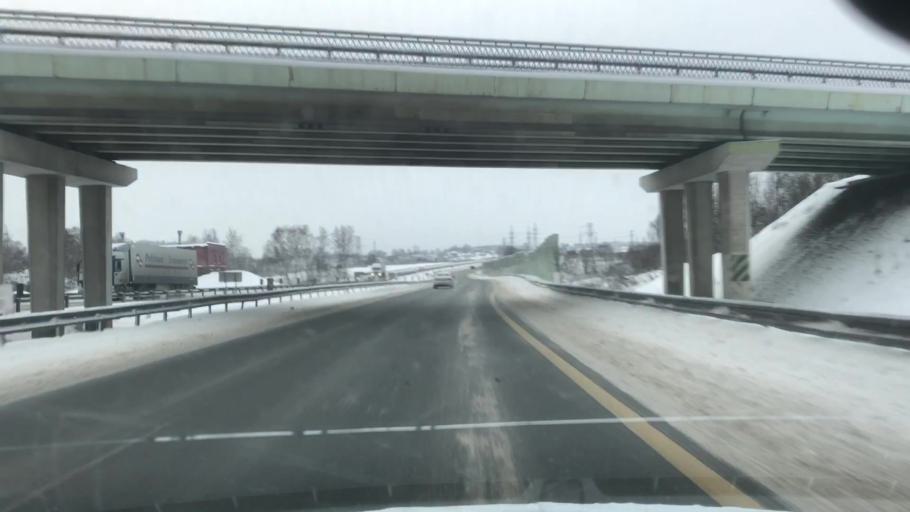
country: RU
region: Moskovskaya
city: Mikhnevo
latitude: 55.1277
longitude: 37.9347
